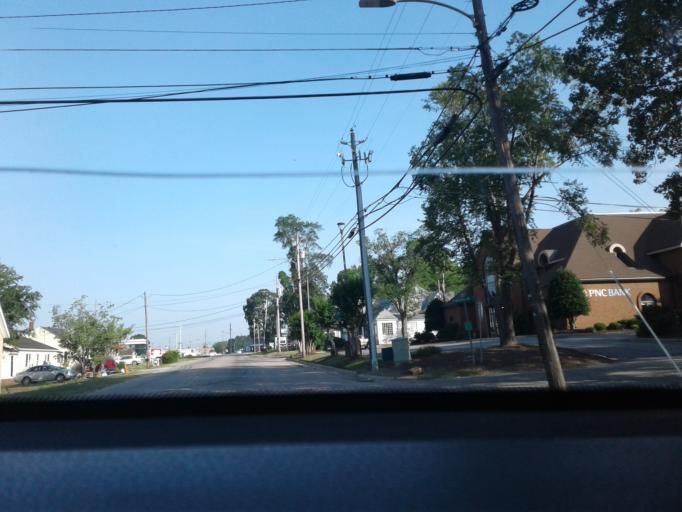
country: US
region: North Carolina
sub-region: Harnett County
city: Dunn
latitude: 35.3144
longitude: -78.6210
